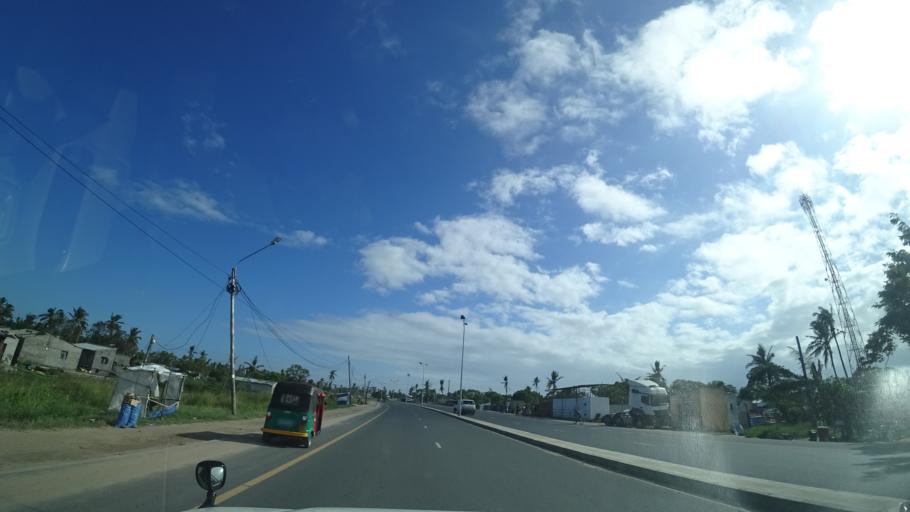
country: MZ
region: Sofala
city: Beira
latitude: -19.7530
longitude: 34.8762
